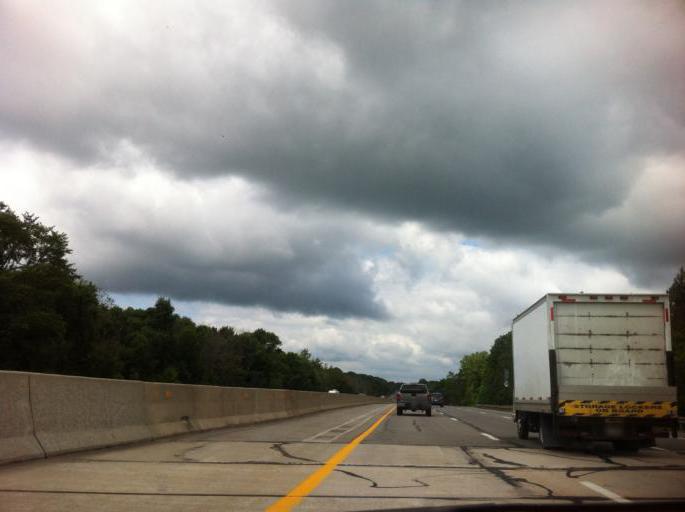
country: US
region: Ohio
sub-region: Portage County
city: Streetsboro
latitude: 41.2548
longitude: -81.3861
